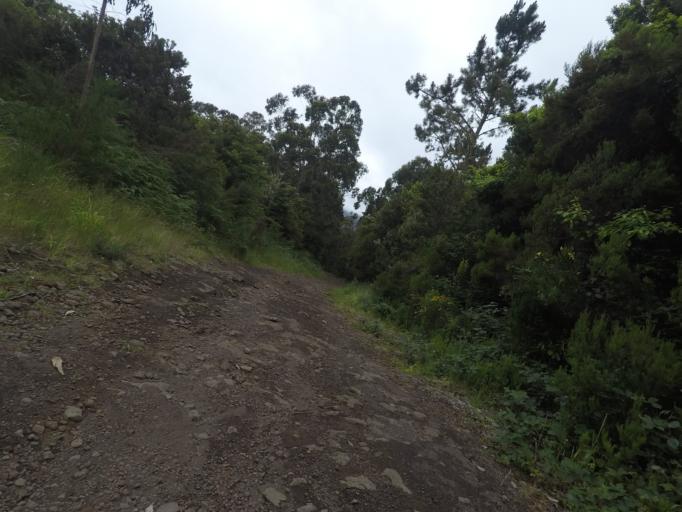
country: PT
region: Madeira
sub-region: Sao Vicente
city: Sao Vicente
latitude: 32.7757
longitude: -17.0522
